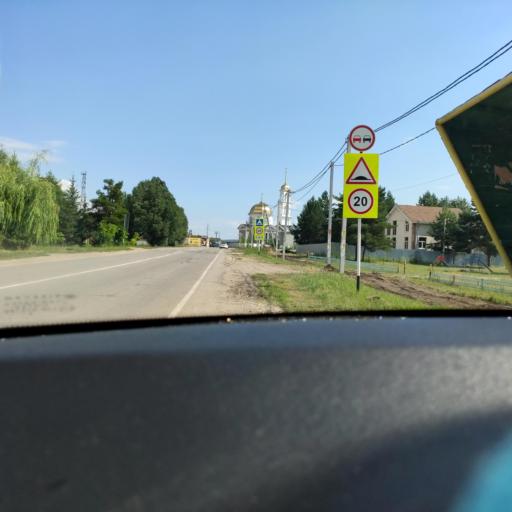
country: RU
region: Samara
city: Volzhskiy
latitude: 53.4494
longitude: 50.1759
